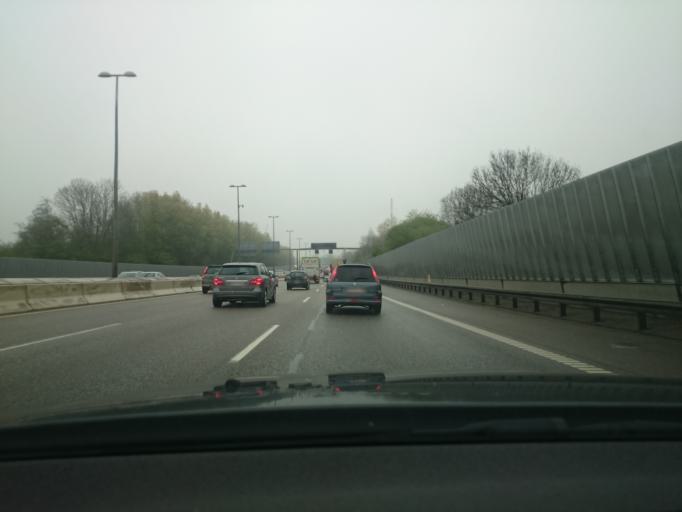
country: DK
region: Capital Region
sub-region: Herlev Kommune
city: Herlev
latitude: 55.7136
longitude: 12.4525
